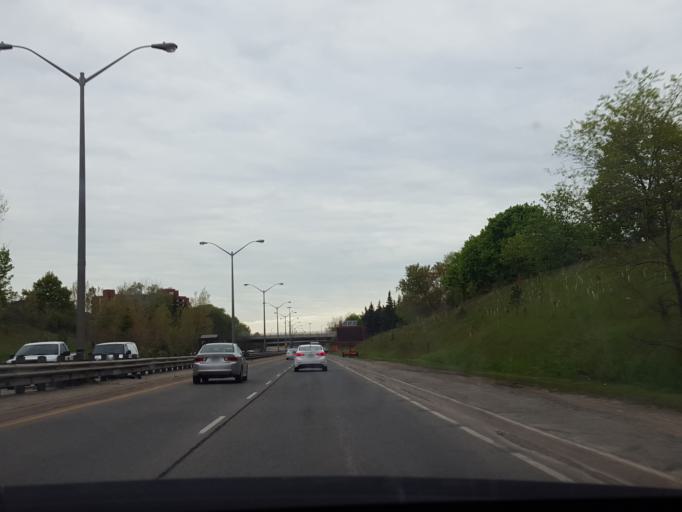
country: CA
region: Ontario
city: Toronto
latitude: 43.7068
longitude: -79.4963
